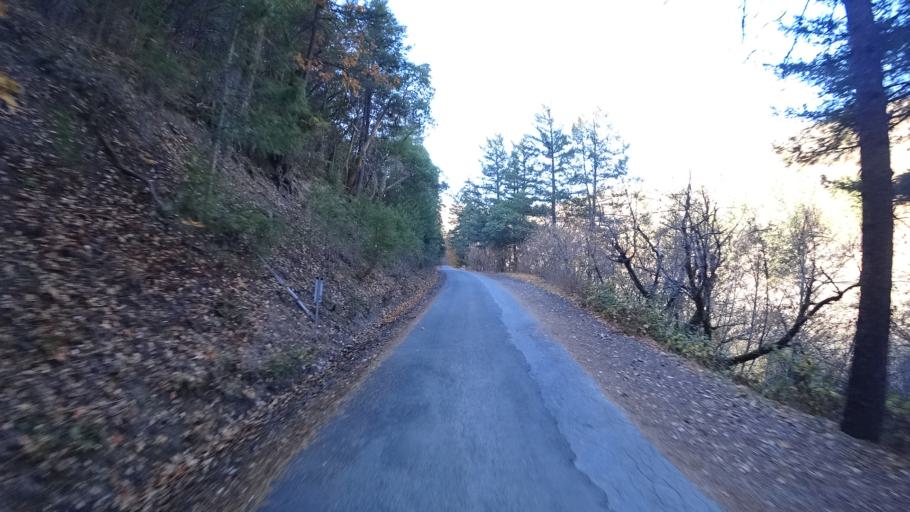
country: US
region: California
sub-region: Siskiyou County
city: Yreka
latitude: 41.8308
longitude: -122.9524
